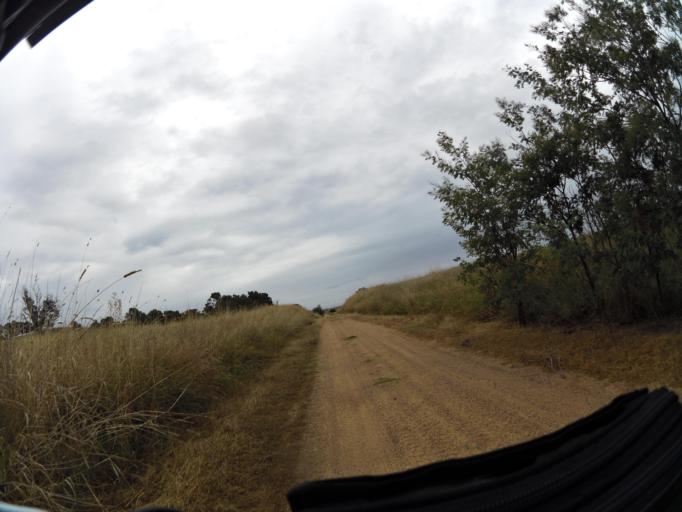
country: AU
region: New South Wales
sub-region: Albury Municipality
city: East Albury
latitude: -36.2065
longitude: 147.0522
